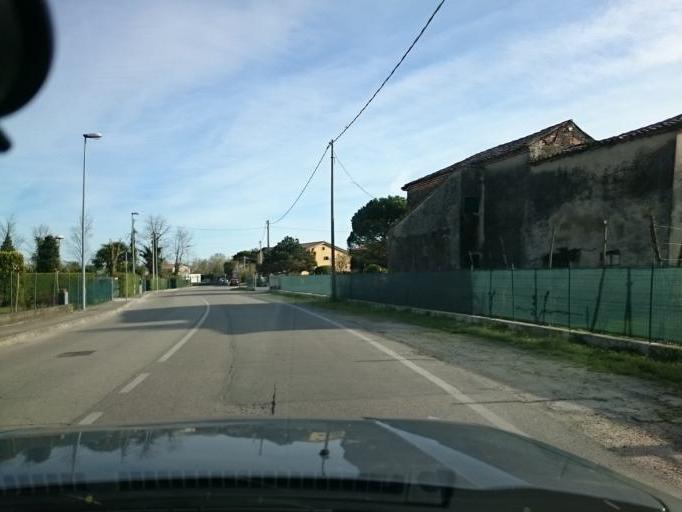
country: IT
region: Veneto
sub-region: Provincia di Padova
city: Mandriola-Sant'Agostino
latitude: 45.3698
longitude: 11.8602
